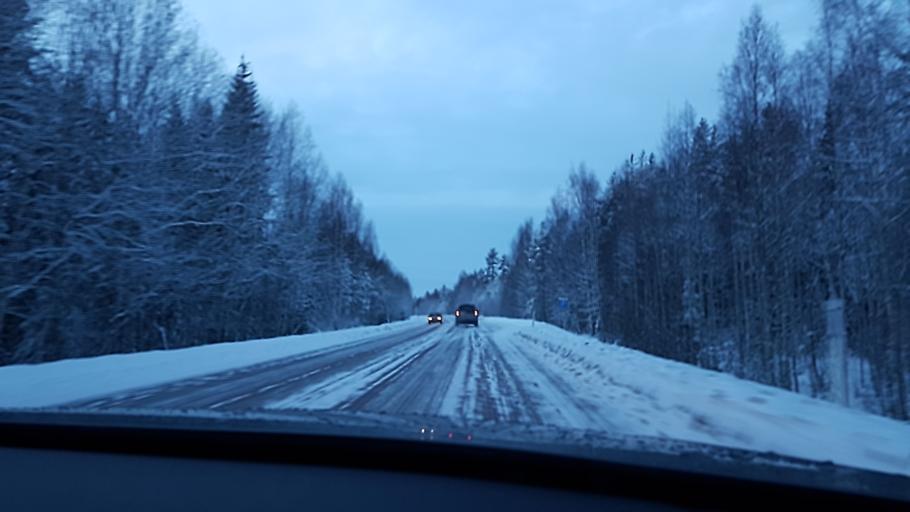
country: SE
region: Jaemtland
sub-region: Harjedalens Kommun
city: Sveg
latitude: 62.0464
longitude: 14.8409
